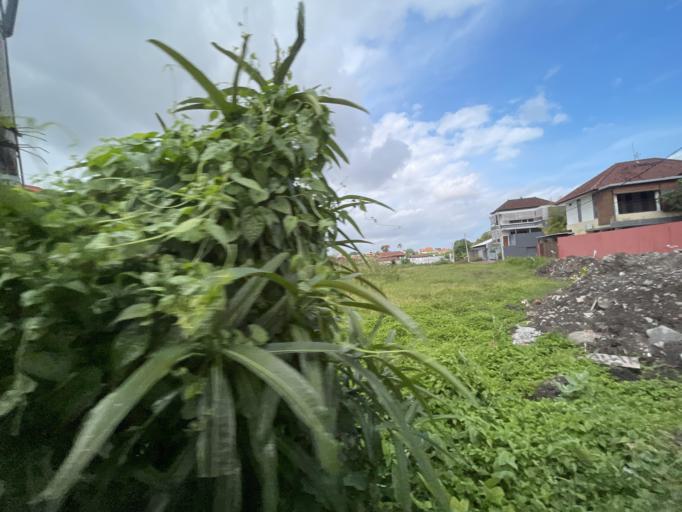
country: ID
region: Bali
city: Kuta
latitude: -8.6734
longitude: 115.1692
